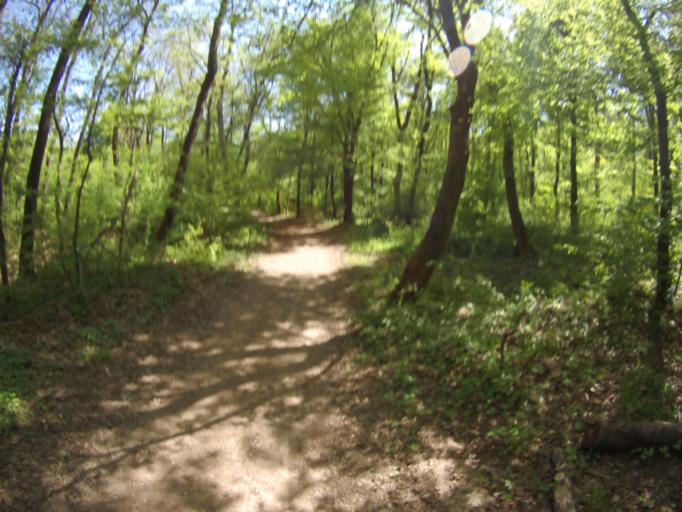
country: HU
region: Pest
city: Budaors
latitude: 47.4858
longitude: 18.9559
